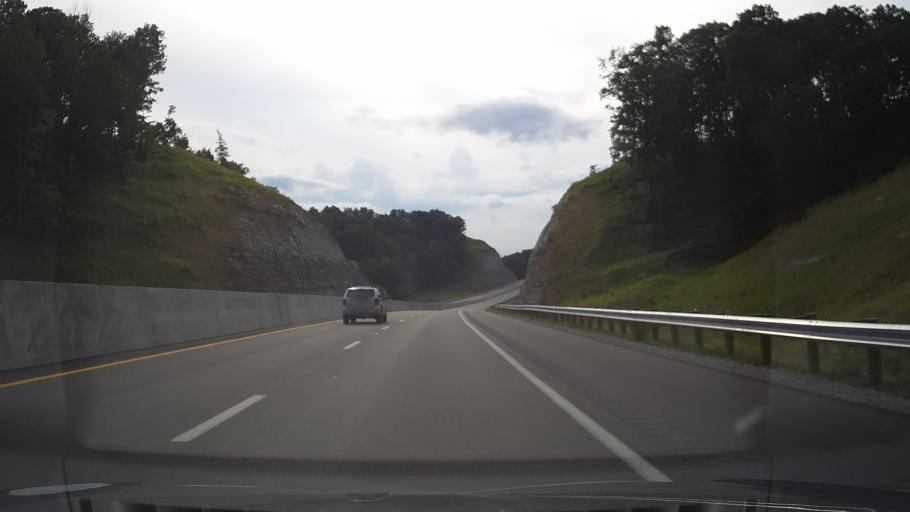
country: US
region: Ohio
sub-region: Scioto County
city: Lucasville
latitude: 38.8694
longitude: -82.9318
